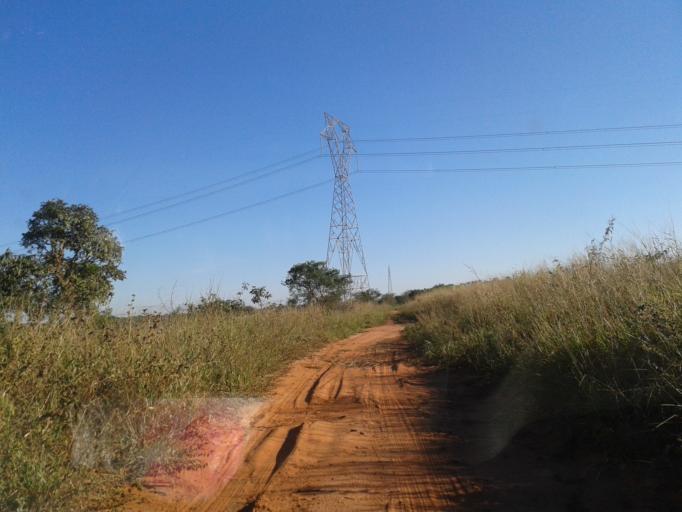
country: BR
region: Minas Gerais
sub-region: Santa Vitoria
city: Santa Vitoria
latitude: -19.0172
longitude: -50.3813
